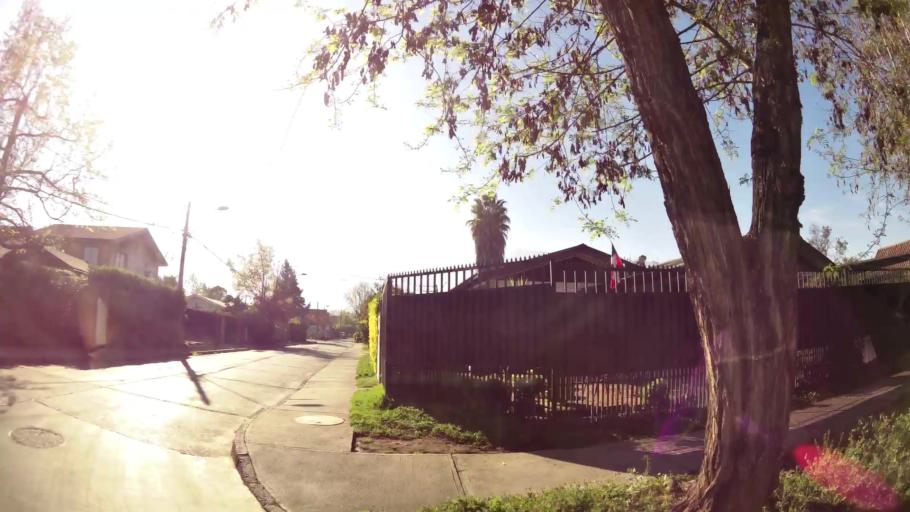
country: CL
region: Santiago Metropolitan
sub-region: Provincia de Santiago
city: Villa Presidente Frei, Nunoa, Santiago, Chile
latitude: -33.4586
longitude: -70.5620
